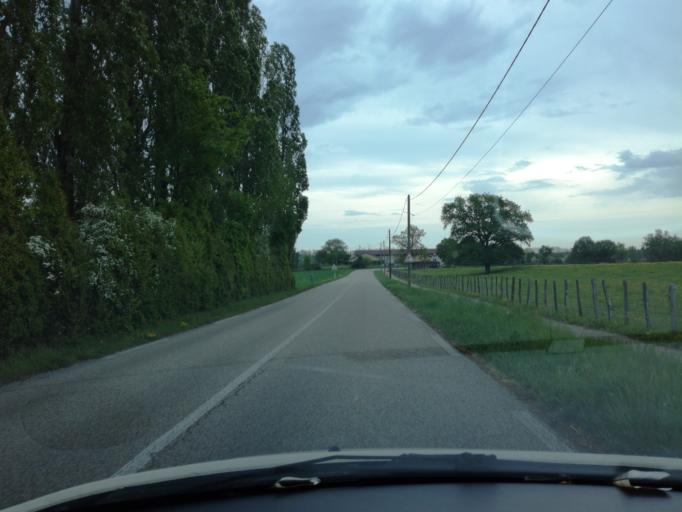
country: FR
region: Rhone-Alpes
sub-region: Departement de l'Ain
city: Peronnas
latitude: 46.1821
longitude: 5.2148
